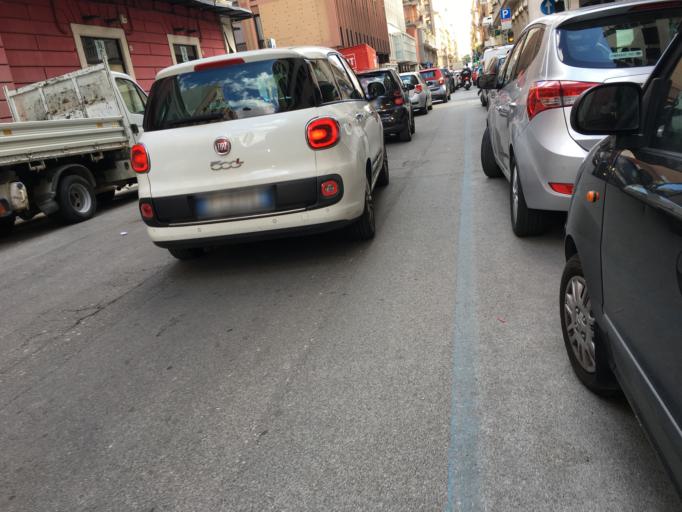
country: IT
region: Apulia
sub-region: Provincia di Bari
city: Bari
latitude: 41.1221
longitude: 16.8701
